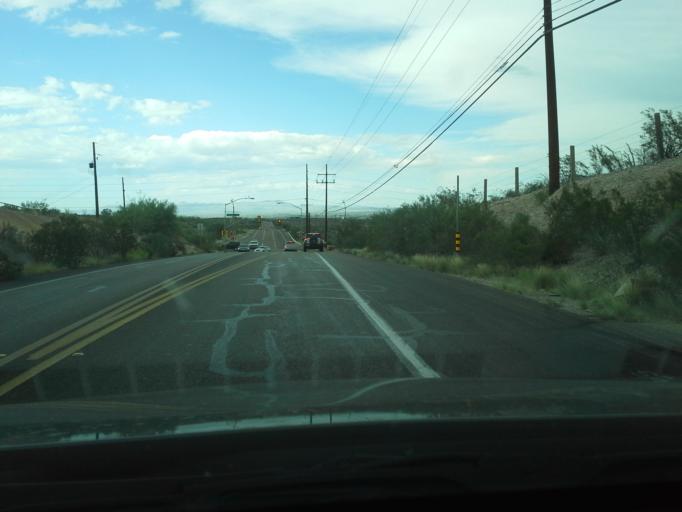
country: US
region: Arizona
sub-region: Pima County
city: South Tucson
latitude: 32.2236
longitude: -111.0203
